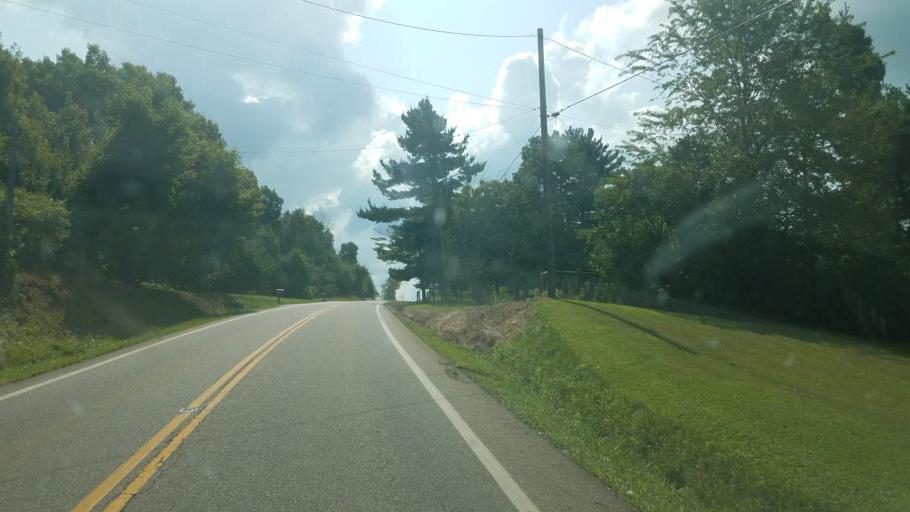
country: US
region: Ohio
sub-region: Columbiana County
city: Lisbon
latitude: 40.7809
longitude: -80.8139
